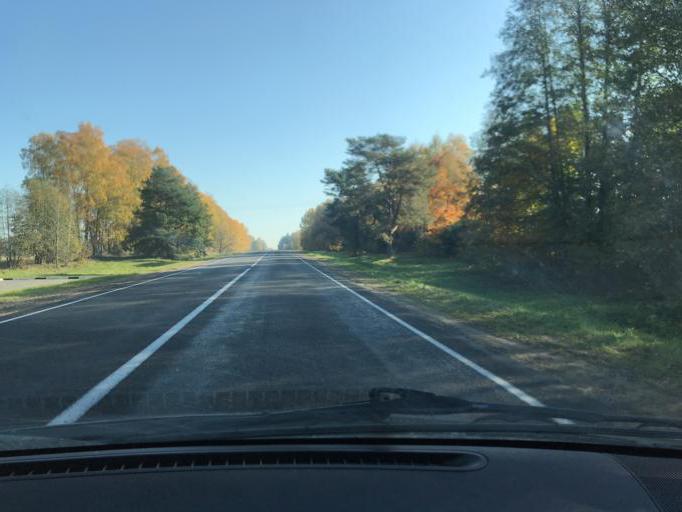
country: BY
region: Brest
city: Lyakhavichy
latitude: 52.9546
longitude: 26.2626
